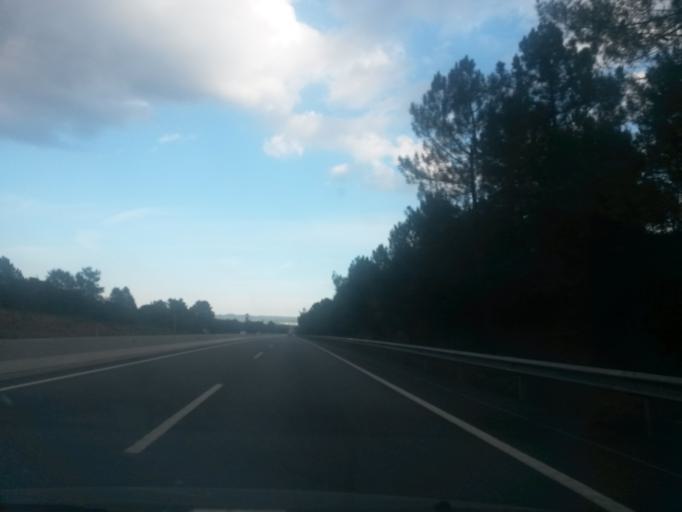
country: ES
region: Catalonia
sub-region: Provincia de Girona
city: Vilobi d'Onyar
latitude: 41.8802
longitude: 2.7144
